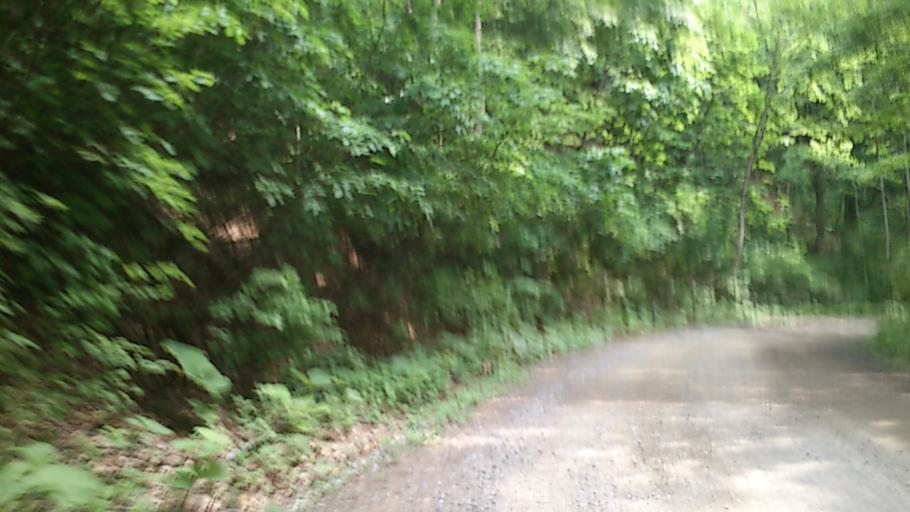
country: JP
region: Aomori
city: Hirosaki
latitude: 40.5565
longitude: 140.1821
